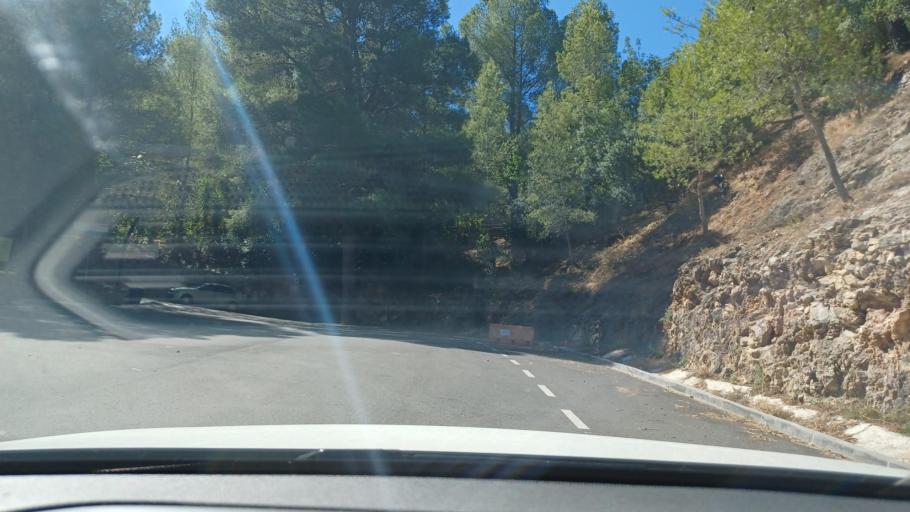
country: ES
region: Catalonia
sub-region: Provincia de Tarragona
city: Benifallet
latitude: 40.9491
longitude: 0.5127
